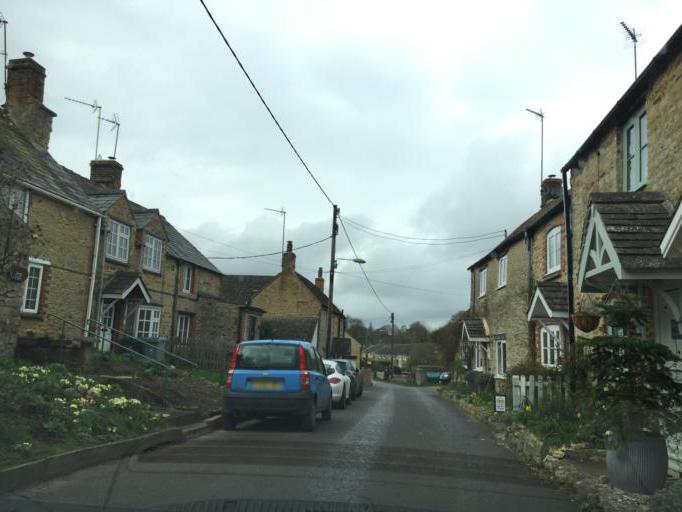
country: GB
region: England
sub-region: Oxfordshire
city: Deddington
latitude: 51.9269
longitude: -1.3655
